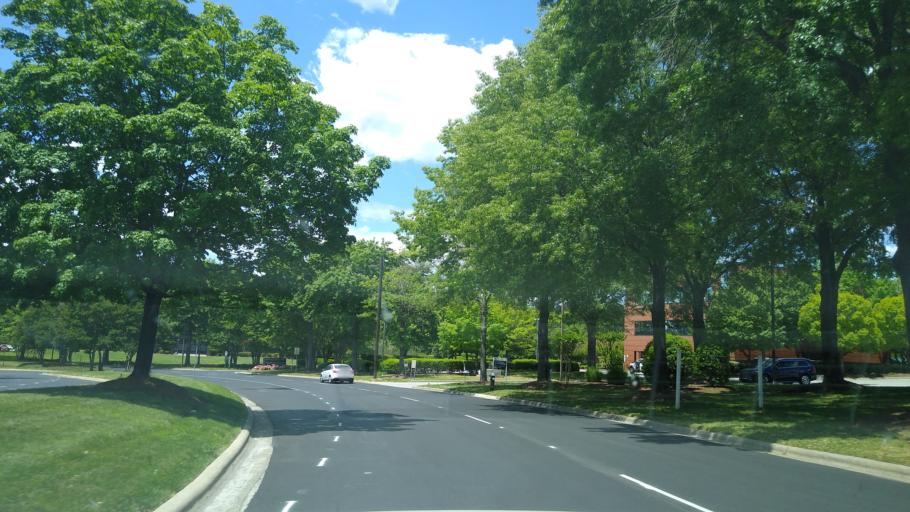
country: US
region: North Carolina
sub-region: Guilford County
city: Greensboro
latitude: 36.0922
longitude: -79.8197
